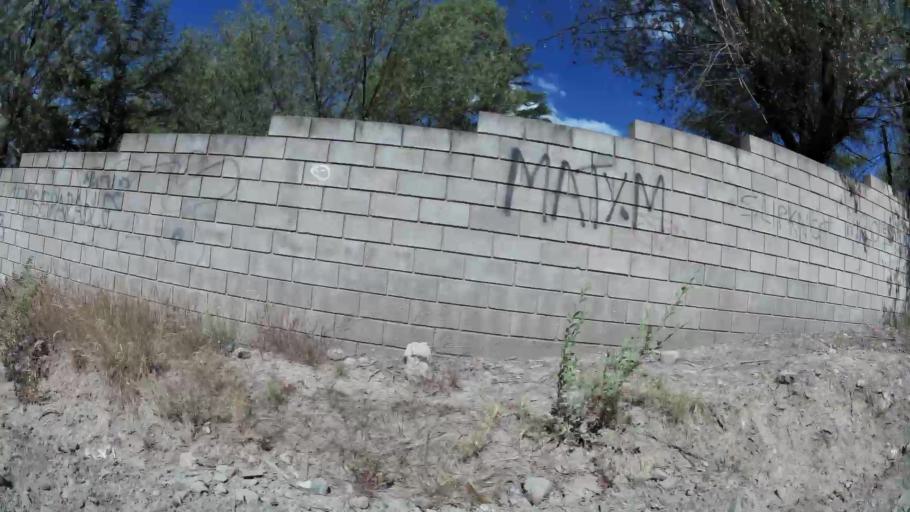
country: AR
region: Cordoba
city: Villa Allende
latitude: -31.2922
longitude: -64.3046
